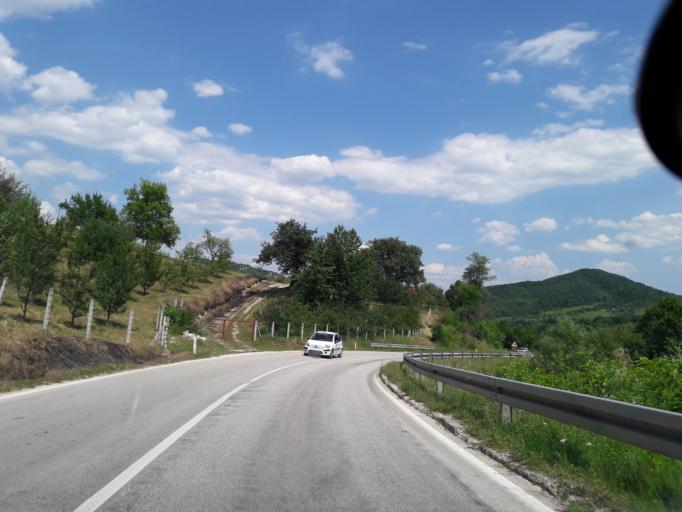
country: BA
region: Republika Srpska
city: Mrkonjic Grad
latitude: 44.4177
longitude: 17.1043
